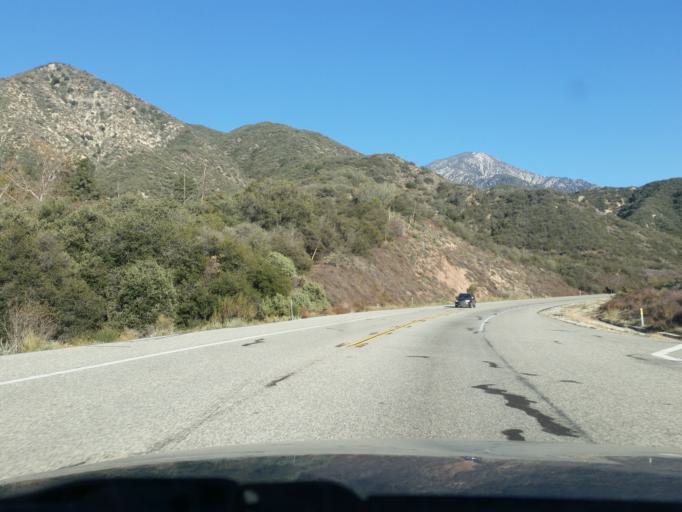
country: US
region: California
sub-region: San Bernardino County
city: Yucaipa
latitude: 34.1042
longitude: -117.0145
